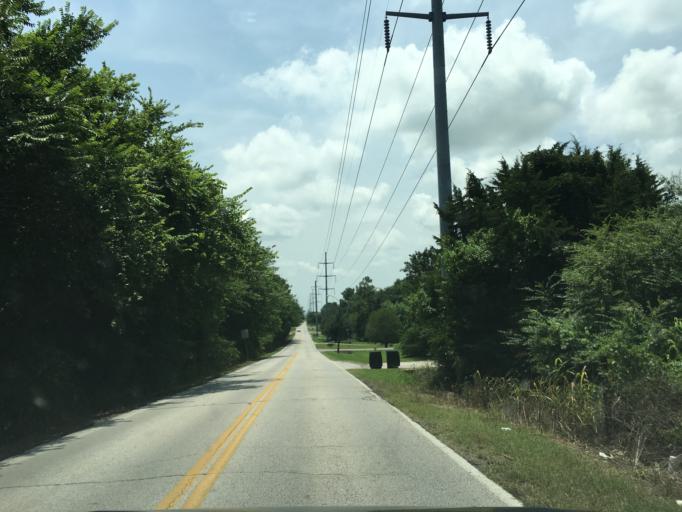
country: US
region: Oklahoma
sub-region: Tulsa County
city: Jenks
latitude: 36.0682
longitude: -95.9938
